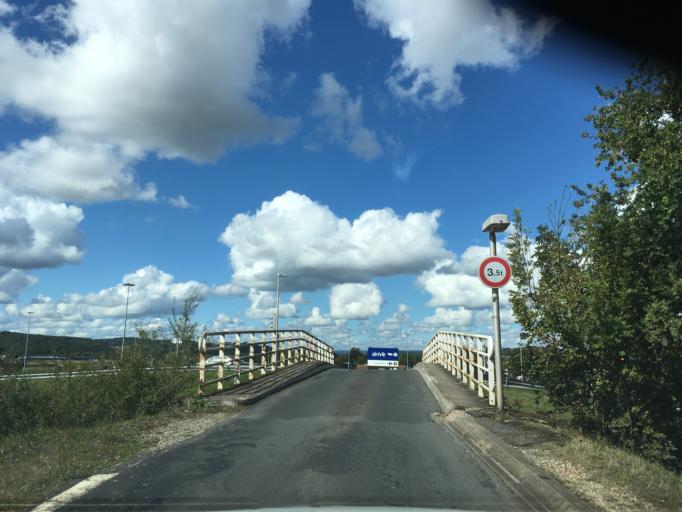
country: FR
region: Limousin
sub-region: Departement de la Correze
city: Saint-Pantaleon-de-Larche
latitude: 45.1436
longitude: 1.4829
